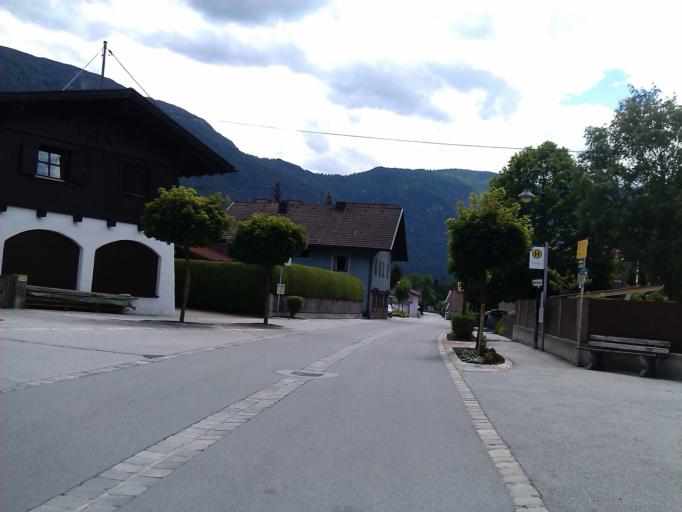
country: AT
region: Tyrol
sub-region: Politischer Bezirk Imst
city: Nassereith
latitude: 47.3121
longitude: 10.8400
